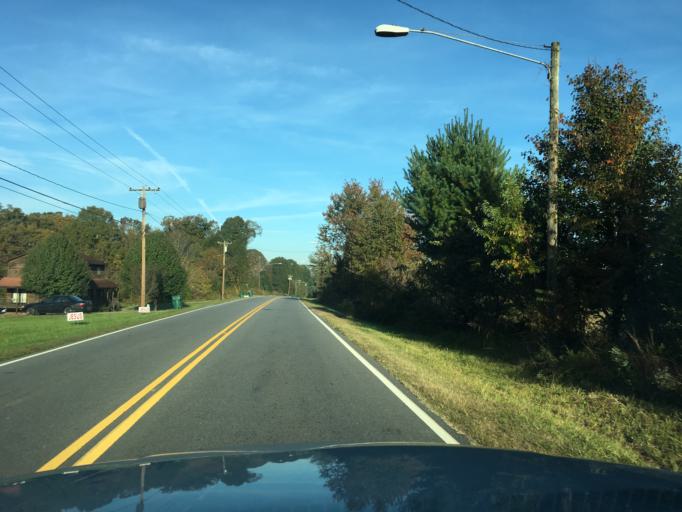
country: US
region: North Carolina
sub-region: Catawba County
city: Newton
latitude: 35.6801
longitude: -81.2444
